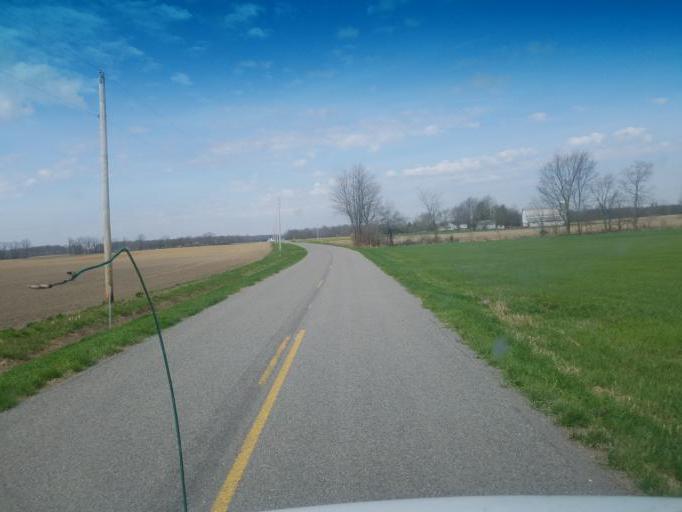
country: US
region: Ohio
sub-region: Logan County
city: Northwood
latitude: 40.4944
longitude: -83.6103
